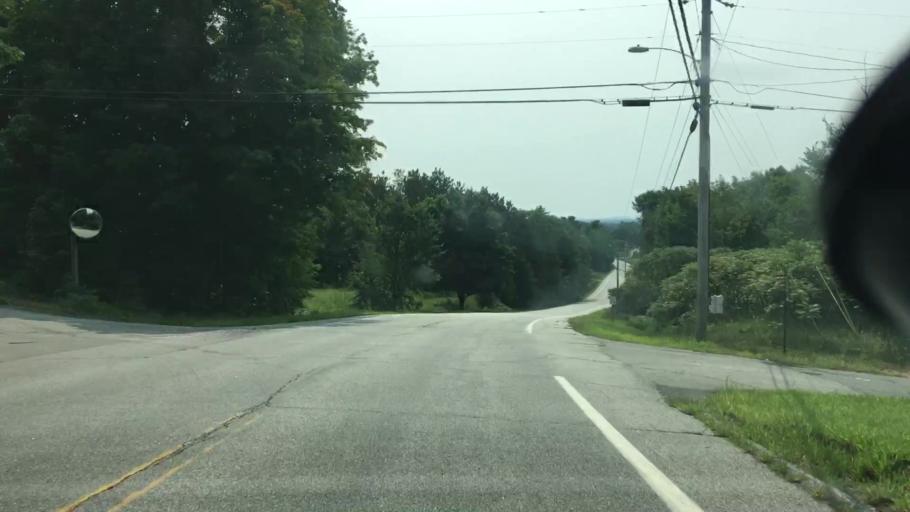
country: US
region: Maine
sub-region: Androscoggin County
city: Livermore Falls
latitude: 44.4227
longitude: -70.1442
